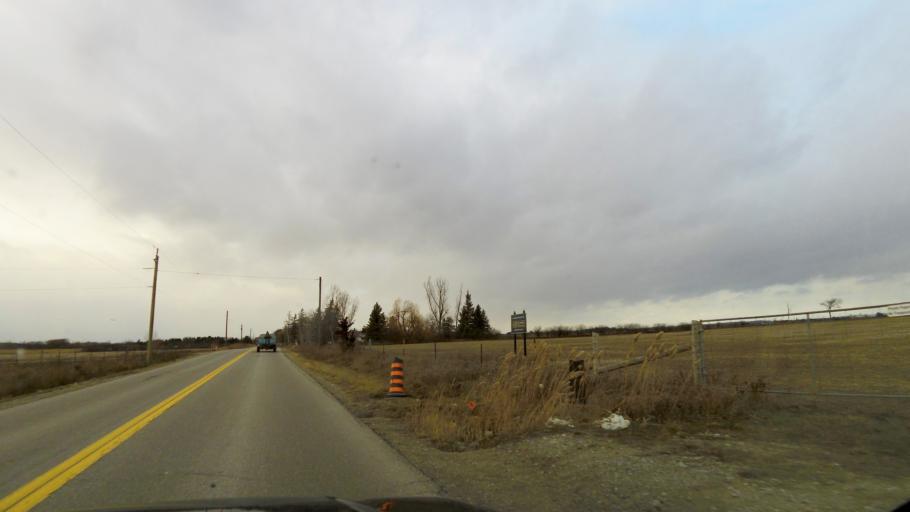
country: CA
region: Ontario
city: Brampton
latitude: 43.8084
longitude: -79.6884
